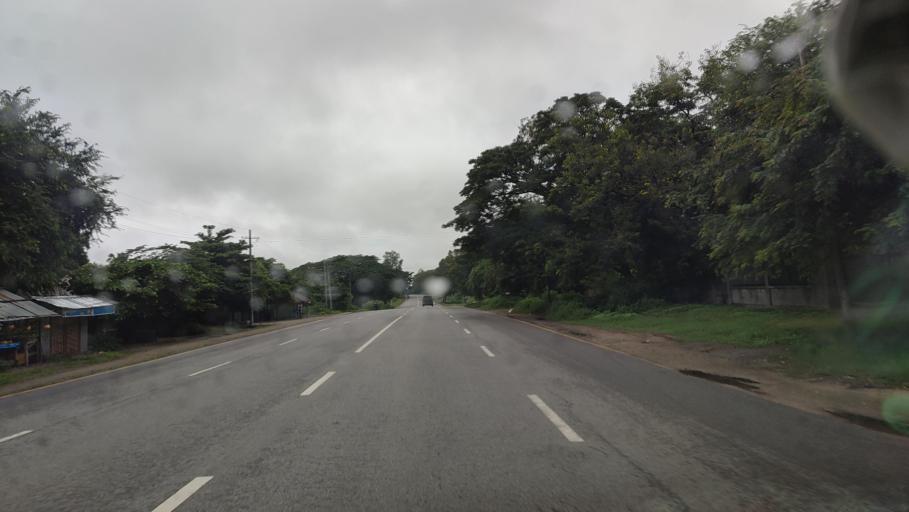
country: MM
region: Mandalay
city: Pyinmana
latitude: 19.9708
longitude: 96.2521
